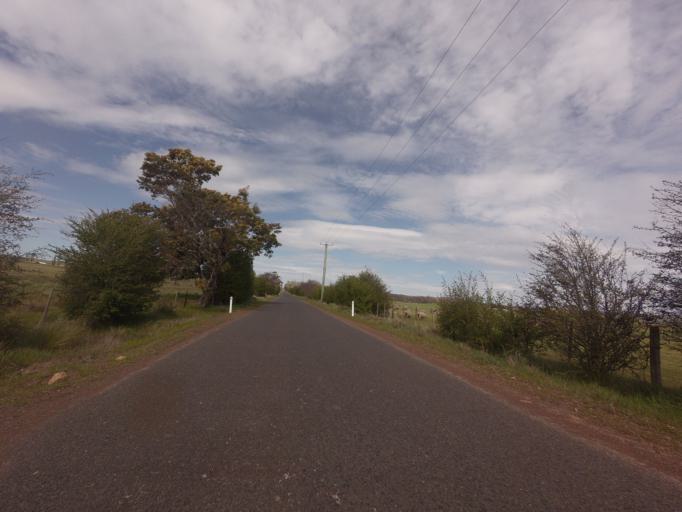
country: AU
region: Tasmania
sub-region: Northern Midlands
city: Evandale
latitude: -41.8749
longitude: 147.3552
